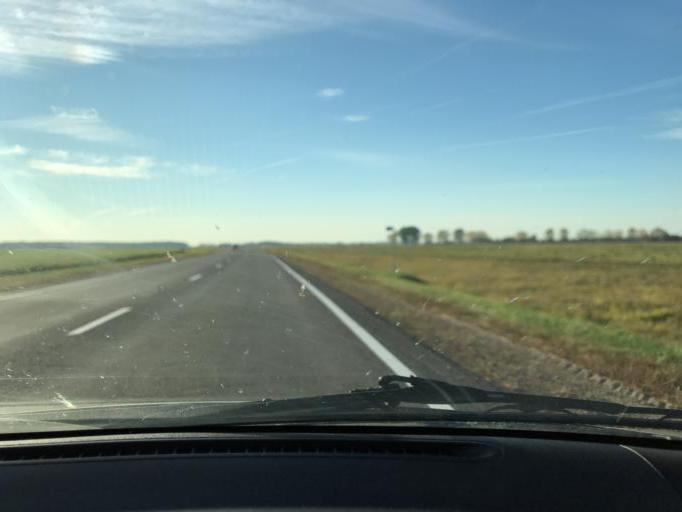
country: BY
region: Brest
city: Antopal'
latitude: 52.2279
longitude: 24.8044
